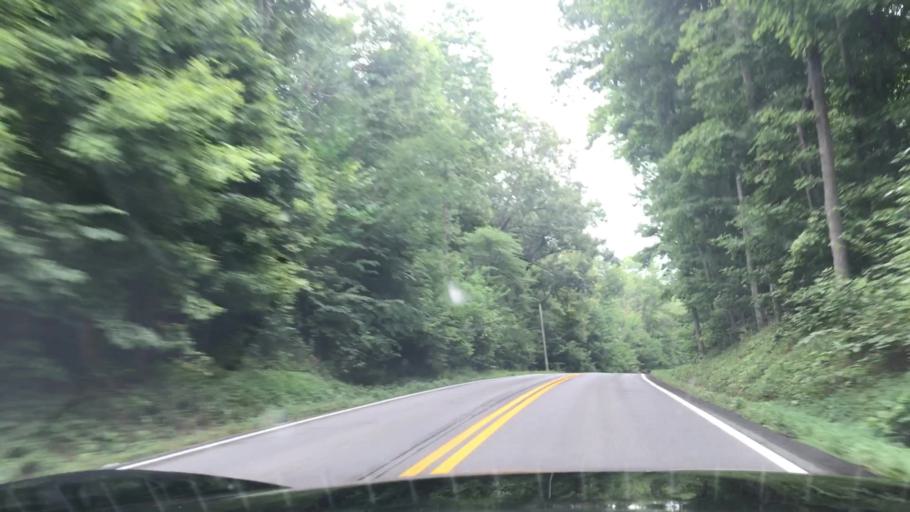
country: US
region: Kentucky
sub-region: Muhlenberg County
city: Central City
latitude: 37.2010
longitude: -87.0282
